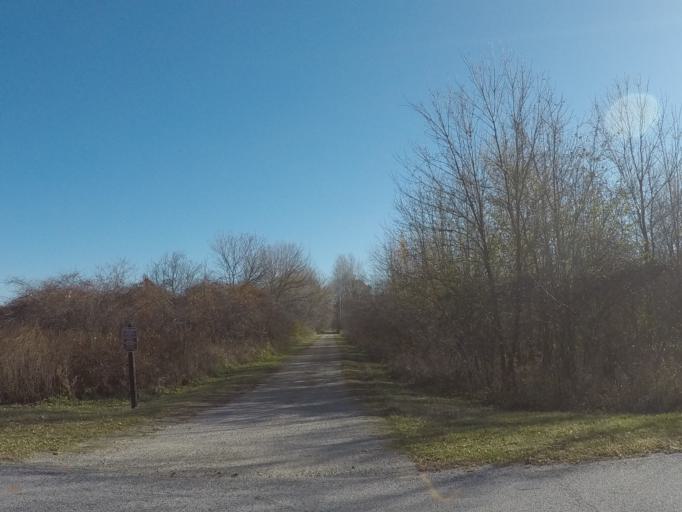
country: US
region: Wisconsin
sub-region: Dane County
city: Deerfield
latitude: 43.0423
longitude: -89.0404
